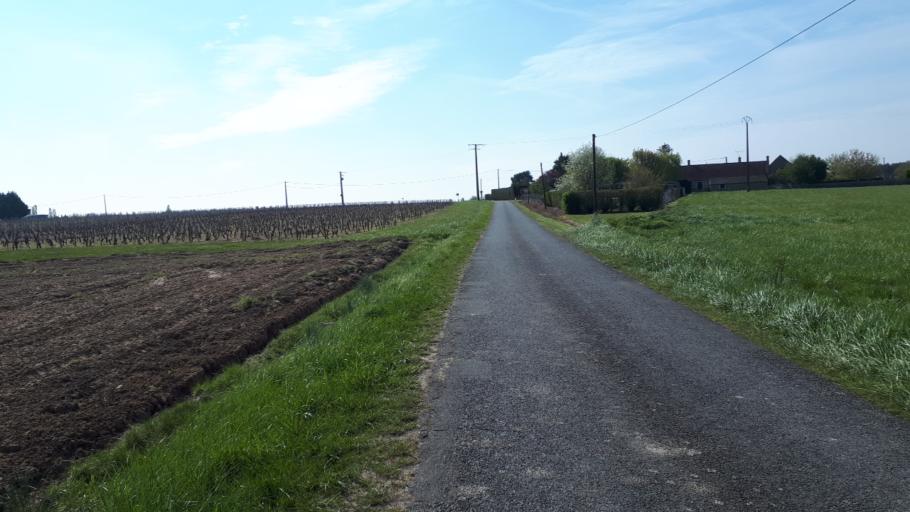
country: FR
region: Centre
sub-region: Departement du Loir-et-Cher
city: Saint-Romain-sur-Cher
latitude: 47.3678
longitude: 1.3899
